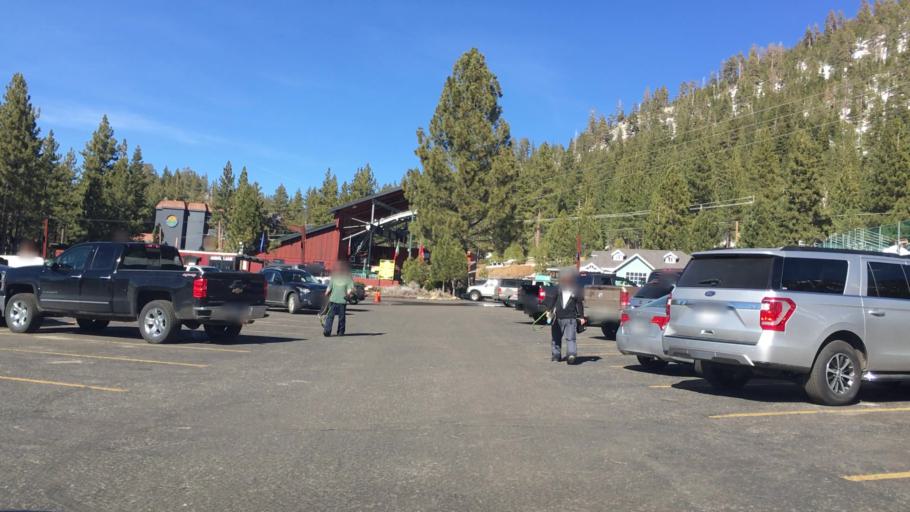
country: US
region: California
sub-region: El Dorado County
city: South Lake Tahoe
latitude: 38.9363
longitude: -119.9396
